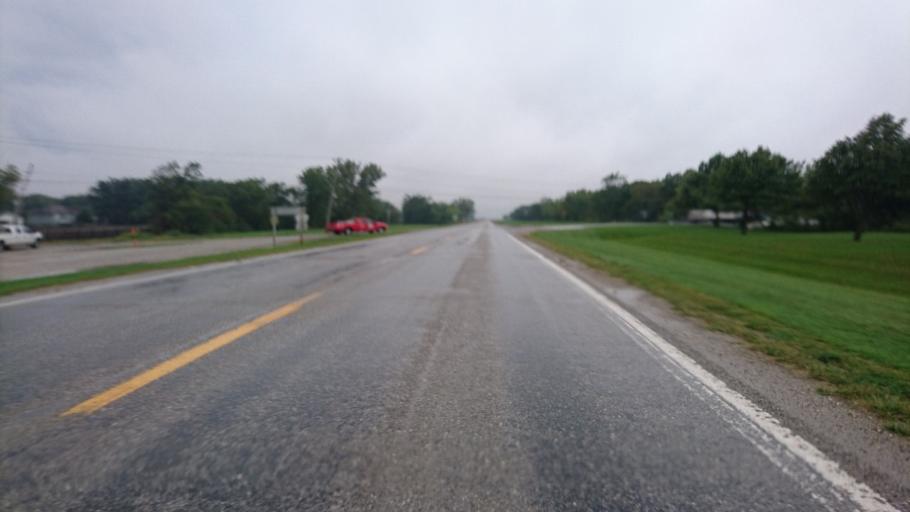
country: US
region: Illinois
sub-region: Sangamon County
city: Williamsville
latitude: 40.0208
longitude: -89.4844
